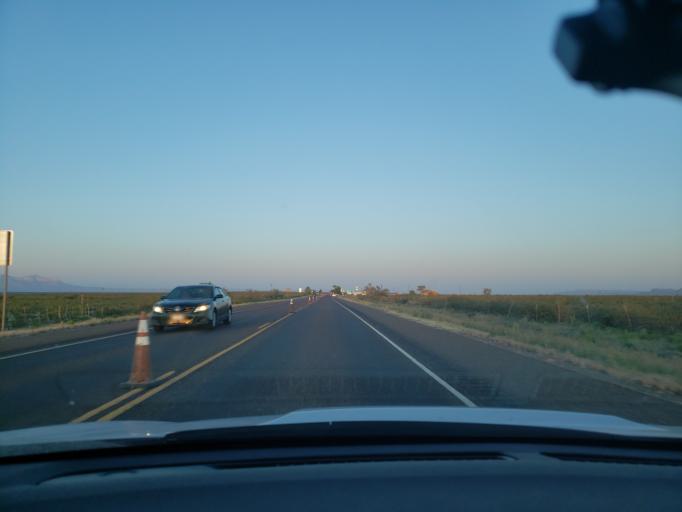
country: US
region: Texas
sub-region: Hudspeth County
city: Sierra Blanca
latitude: 31.7622
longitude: -105.3721
